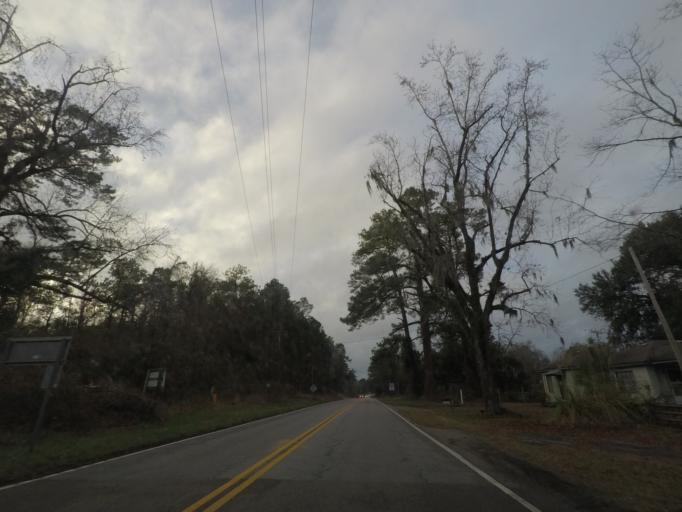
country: US
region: South Carolina
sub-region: Dorchester County
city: Saint George
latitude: 33.0570
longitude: -80.6208
